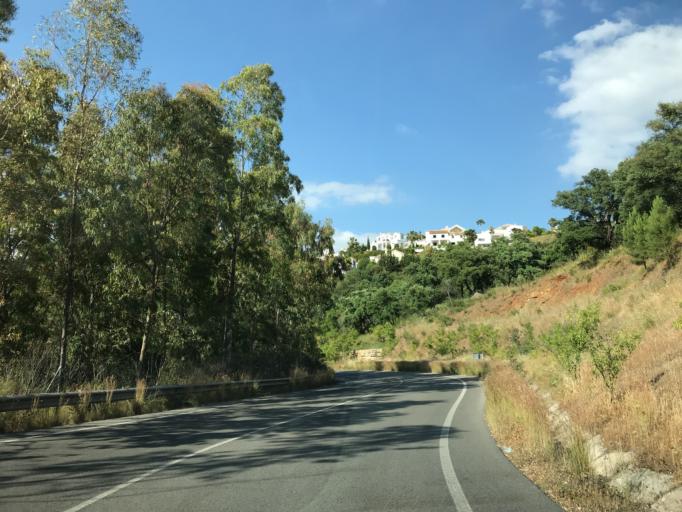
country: ES
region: Andalusia
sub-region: Provincia de Malaga
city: Benahavis
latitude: 36.5038
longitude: -5.0141
